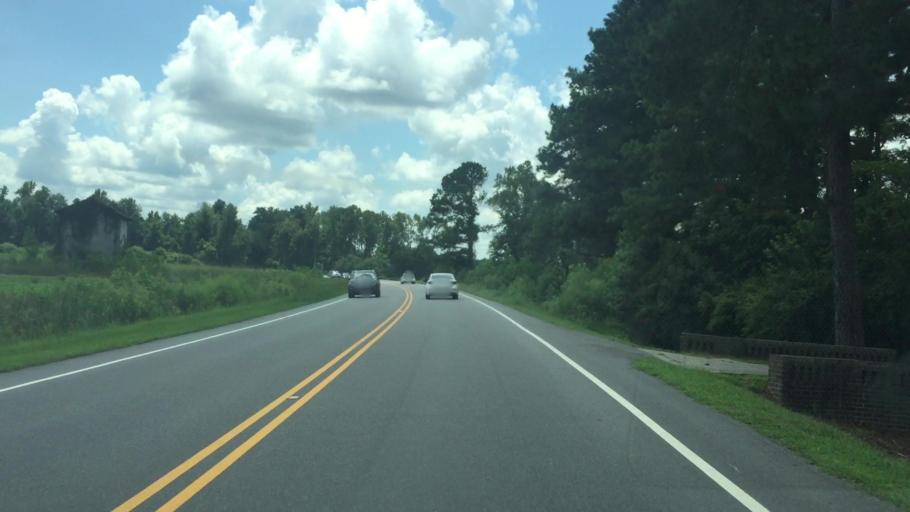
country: US
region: North Carolina
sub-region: Columbus County
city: Tabor City
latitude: 34.1988
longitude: -78.8342
